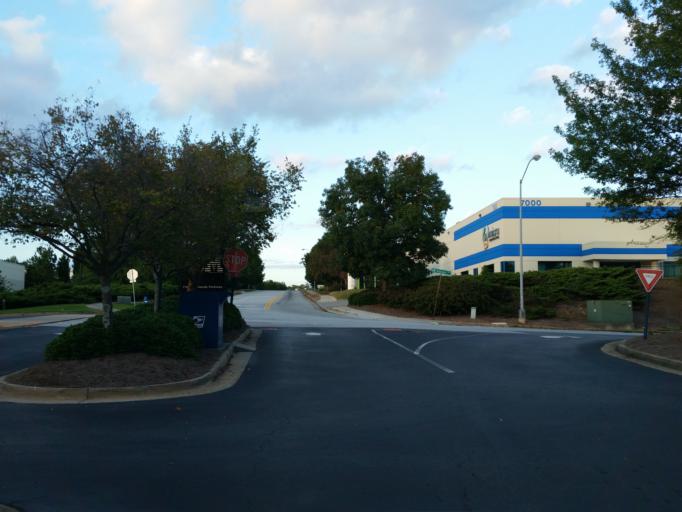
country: US
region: Georgia
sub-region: Cobb County
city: Smyrna
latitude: 33.8368
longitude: -84.5209
